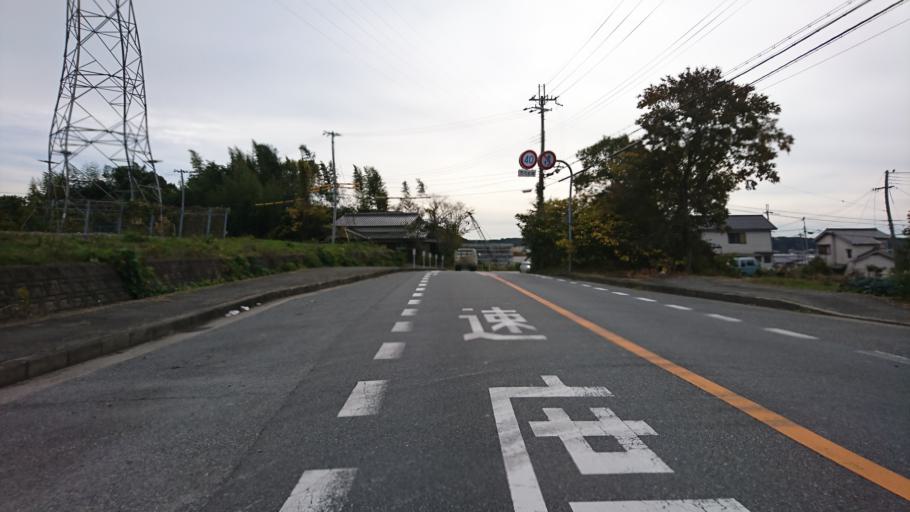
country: JP
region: Hyogo
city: Ono
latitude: 34.7950
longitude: 134.9237
